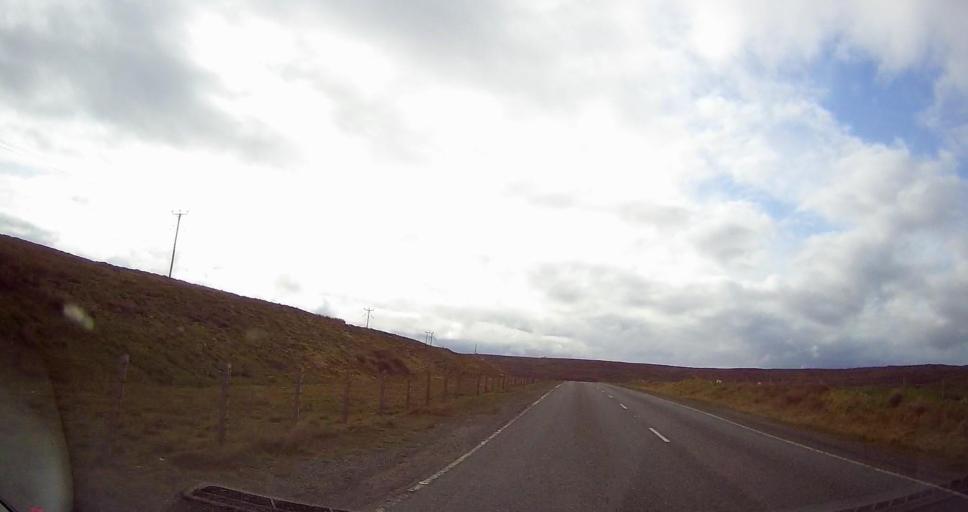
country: GB
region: Scotland
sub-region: Shetland Islands
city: Lerwick
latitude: 60.4428
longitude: -1.2341
